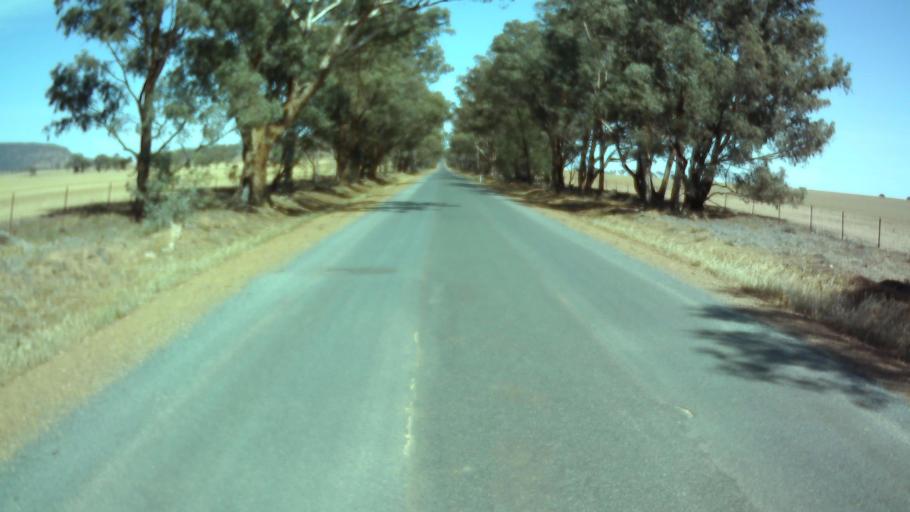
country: AU
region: New South Wales
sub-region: Weddin
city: Grenfell
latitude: -33.8633
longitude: 148.0306
